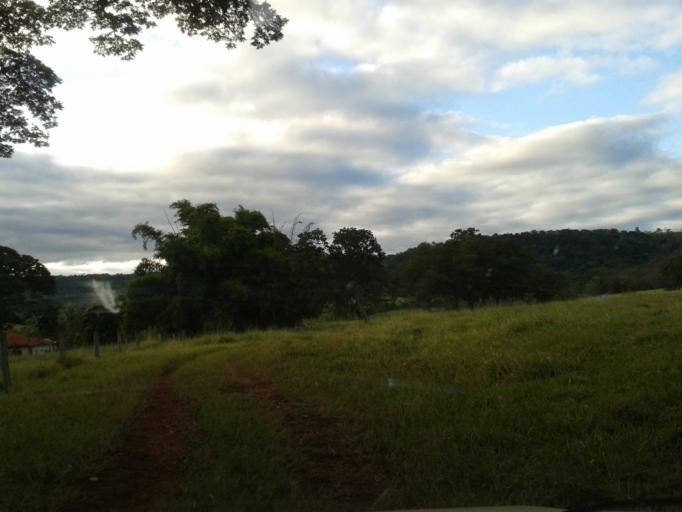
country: BR
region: Minas Gerais
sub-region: Campina Verde
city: Campina Verde
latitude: -19.4630
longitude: -49.6530
